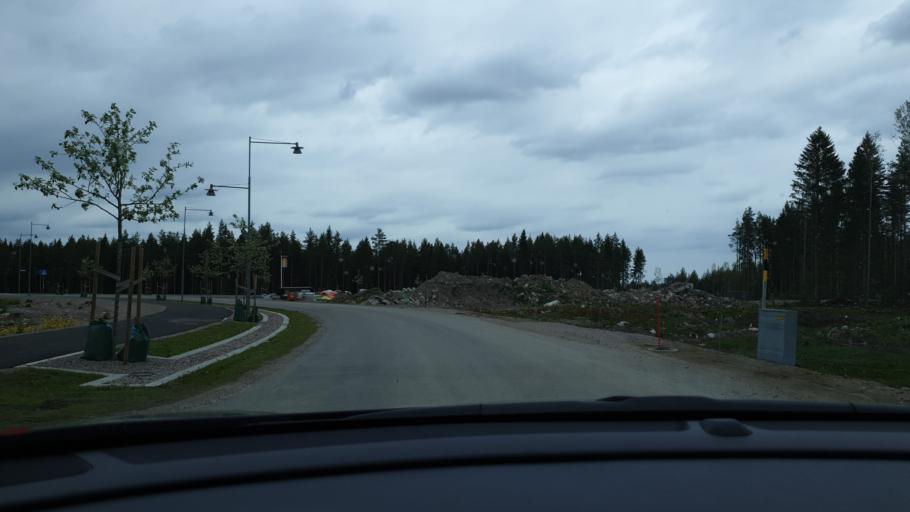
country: SE
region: Gaevleborg
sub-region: Gavle Kommun
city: Gavle
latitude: 60.6410
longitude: 17.1537
